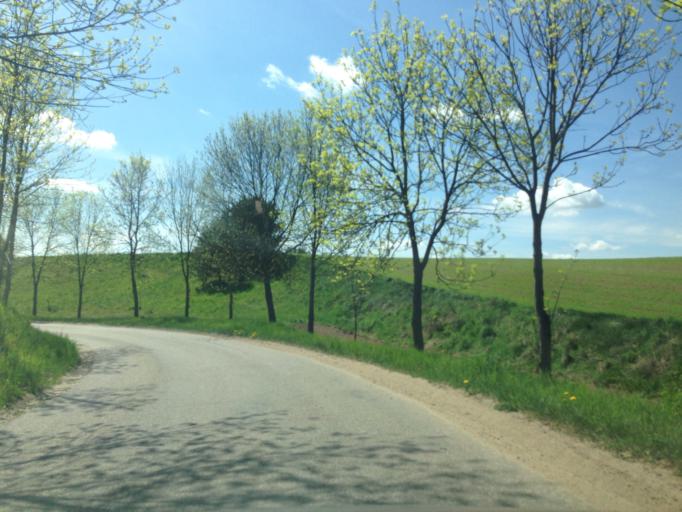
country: PL
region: Kujawsko-Pomorskie
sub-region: Powiat brodnicki
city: Bartniczka
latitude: 53.2845
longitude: 19.6553
